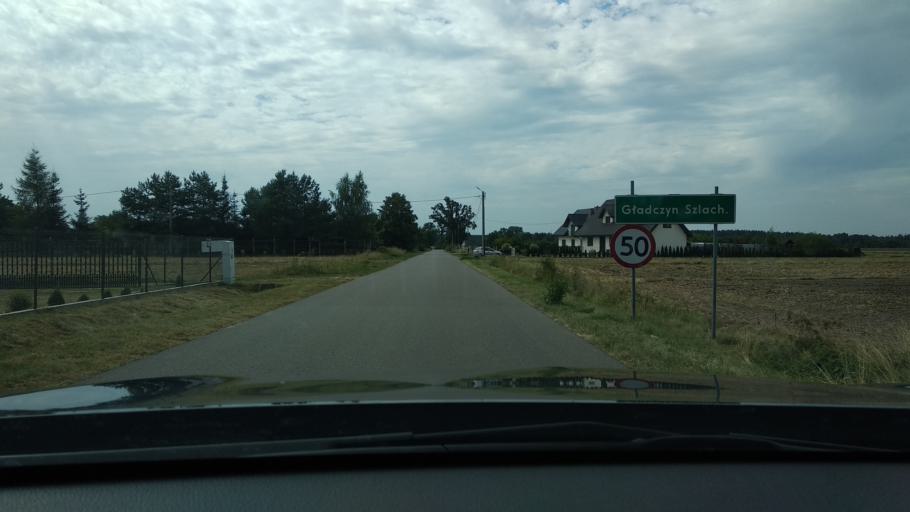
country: PL
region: Masovian Voivodeship
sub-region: Powiat pultuski
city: Zatory
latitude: 52.6538
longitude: 21.1866
